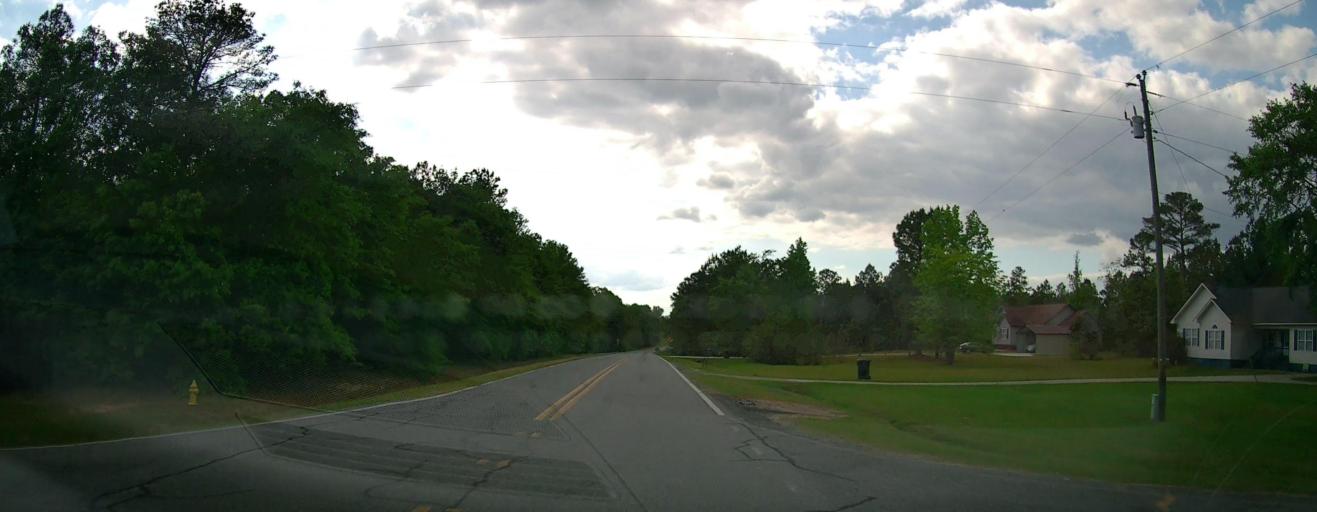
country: US
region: Georgia
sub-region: Baldwin County
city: Hardwick
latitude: 33.0605
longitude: -83.1319
